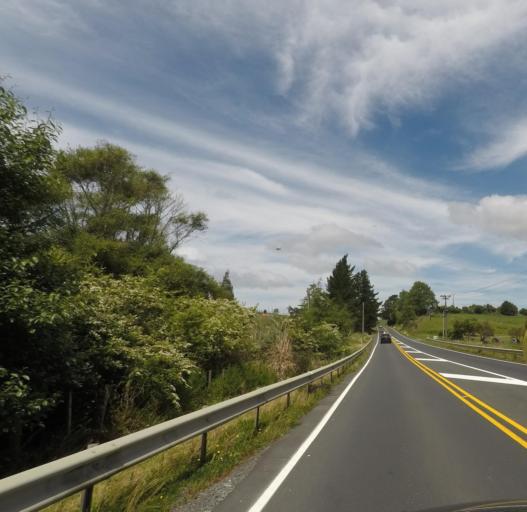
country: NZ
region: Auckland
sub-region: Auckland
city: Rothesay Bay
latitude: -36.6614
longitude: 174.6730
